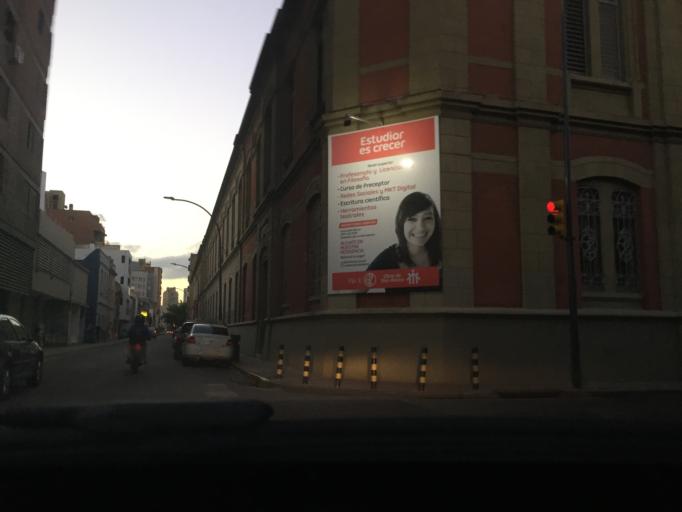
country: AR
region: Cordoba
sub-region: Departamento de Capital
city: Cordoba
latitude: -31.4109
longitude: -64.1970
